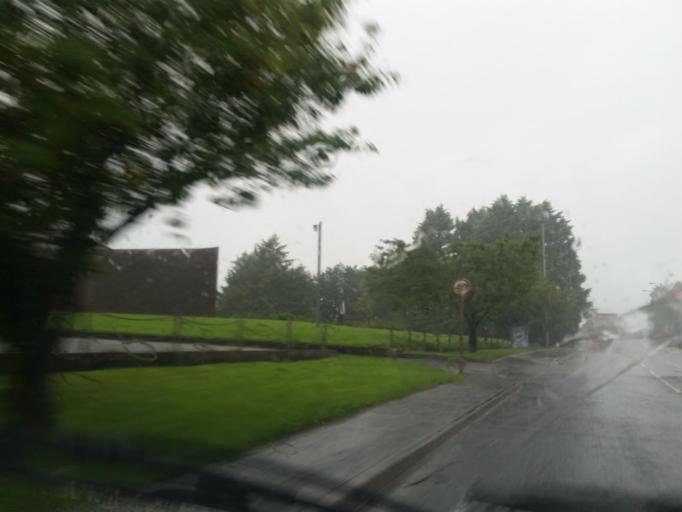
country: GB
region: Northern Ireland
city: Fivemiletown
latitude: 54.4149
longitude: -7.1633
